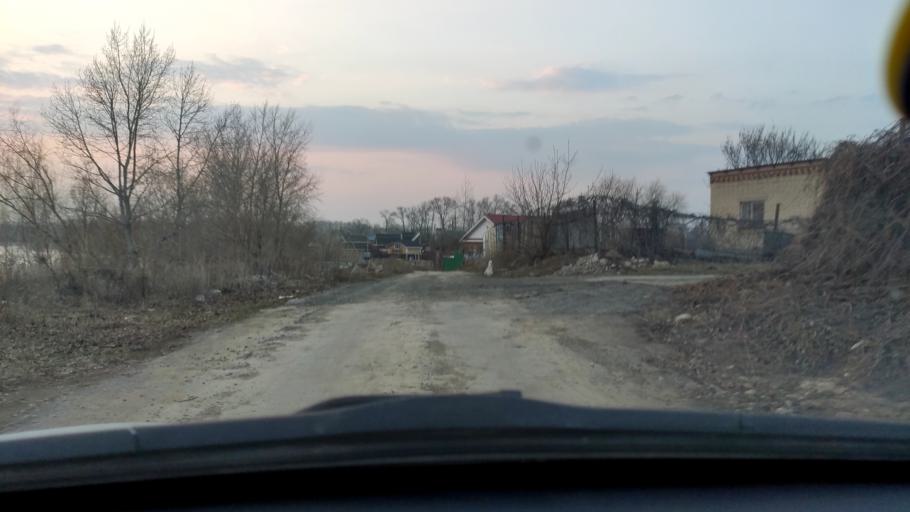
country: RU
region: Samara
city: Zhigulevsk
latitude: 53.4541
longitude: 49.5189
